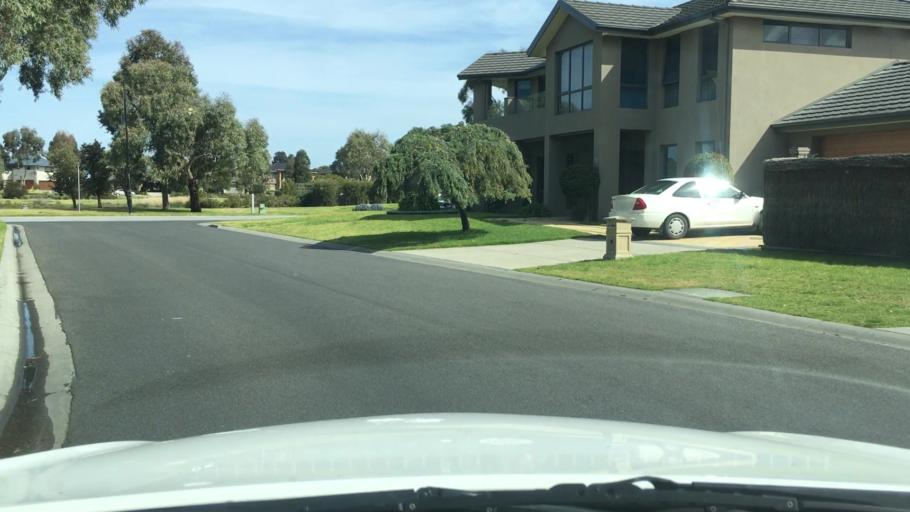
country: AU
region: Victoria
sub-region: Kingston
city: Waterways
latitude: -38.0146
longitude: 145.1341
